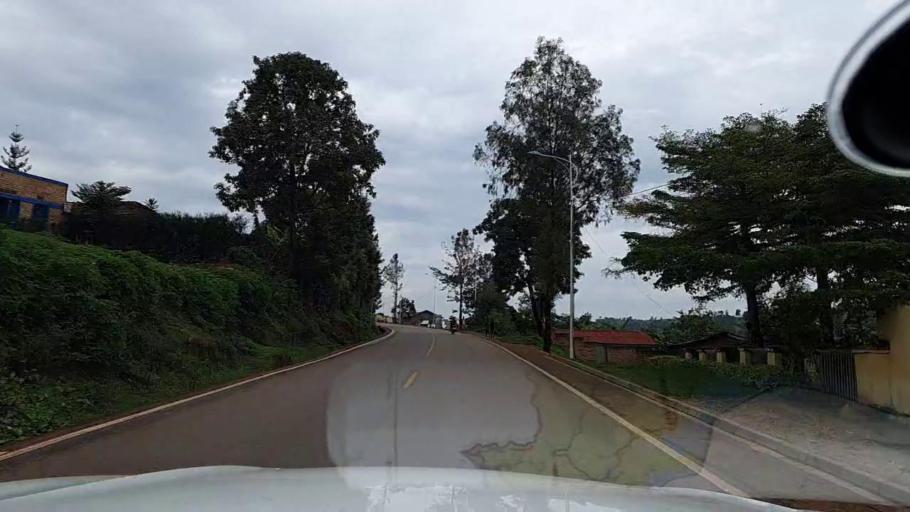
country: RW
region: Southern Province
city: Butare
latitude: -2.5825
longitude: 29.7365
